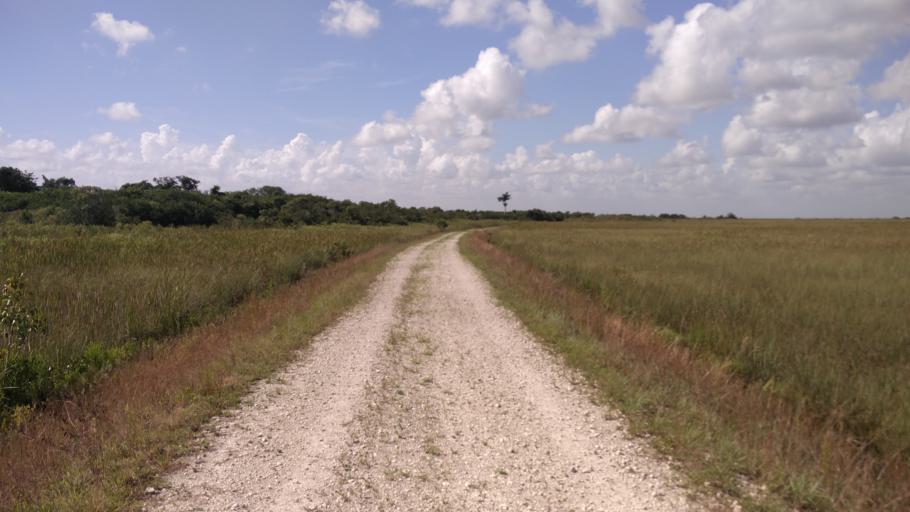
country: US
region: Florida
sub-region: Broward County
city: Weston
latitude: 26.0534
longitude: -80.4620
